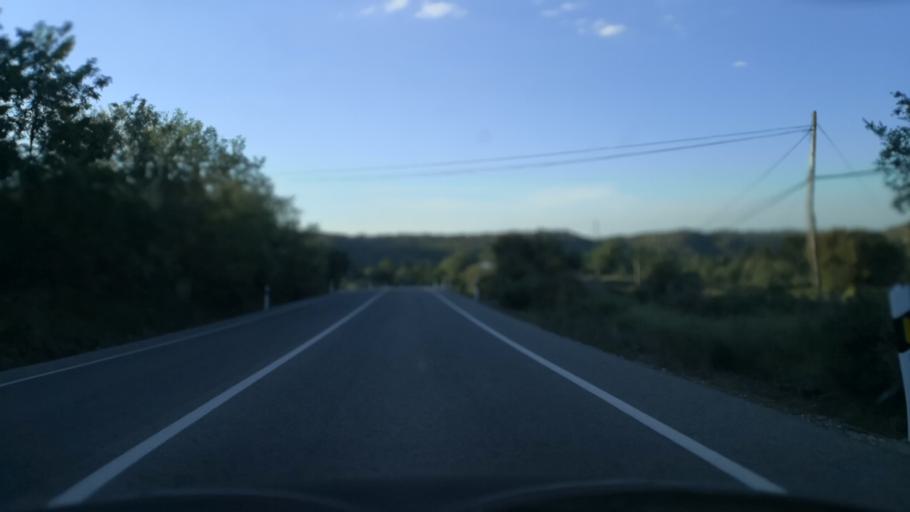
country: PT
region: Portalegre
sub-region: Portalegre
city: Sao Juliao
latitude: 39.3571
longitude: -7.2751
